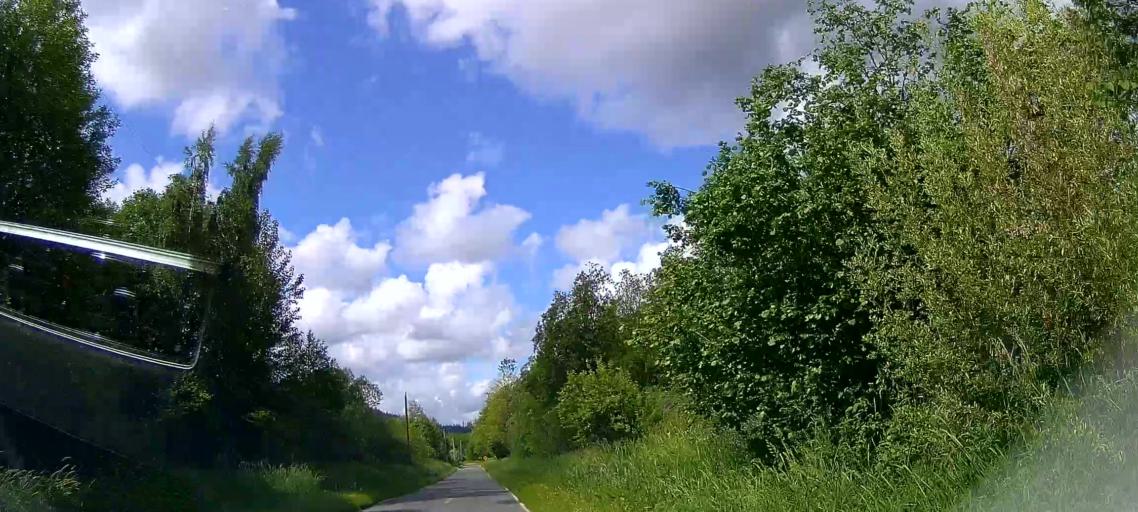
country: US
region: Washington
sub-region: Whatcom County
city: Sudden Valley
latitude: 48.6576
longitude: -122.2040
